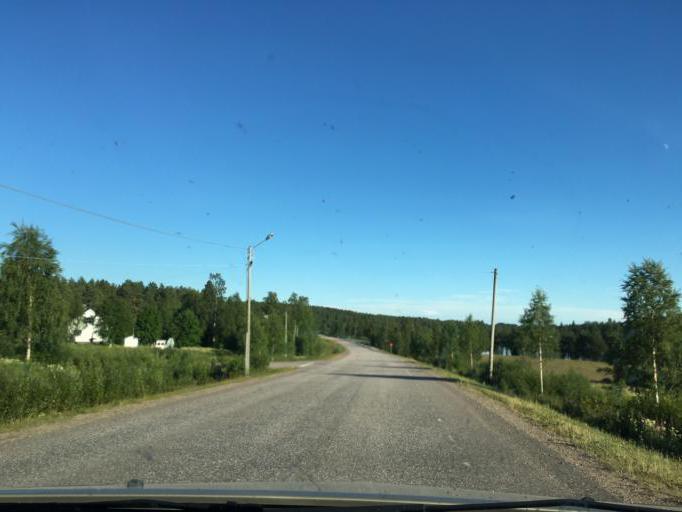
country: SE
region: Norrbotten
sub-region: Kalix Kommun
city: Rolfs
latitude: 65.9198
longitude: 22.9150
